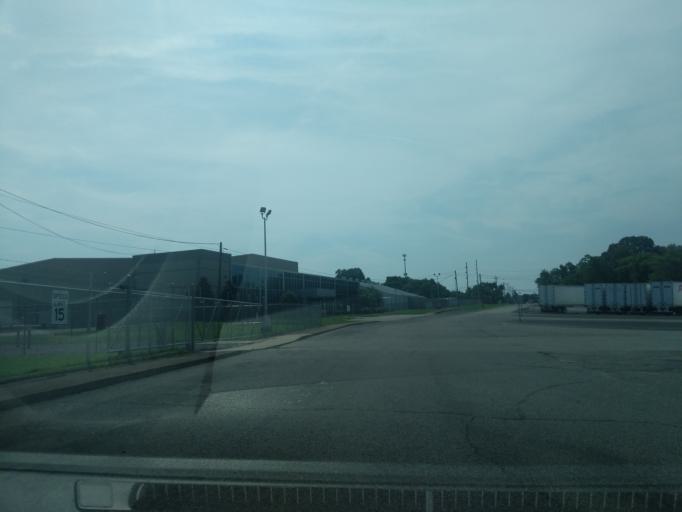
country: US
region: Tennessee
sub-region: Davidson County
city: Lakewood
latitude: 36.2683
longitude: -86.6539
